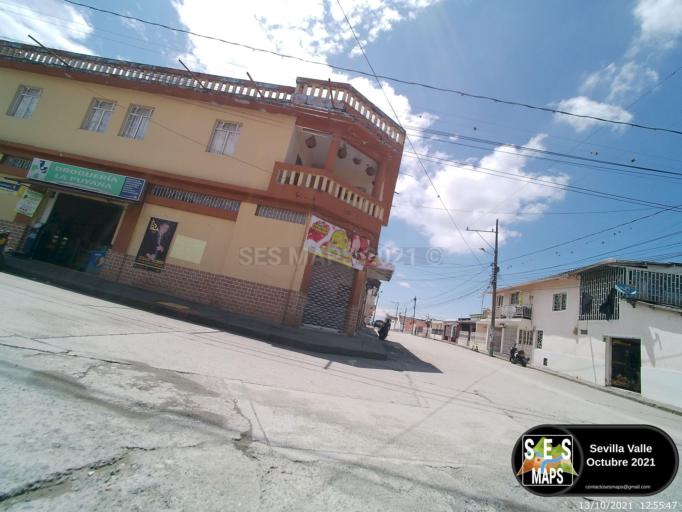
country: CO
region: Valle del Cauca
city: Sevilla
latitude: 4.2730
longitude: -75.9318
